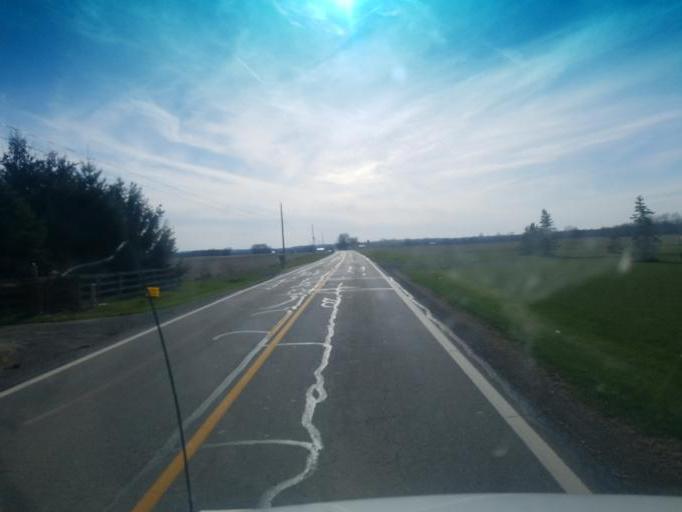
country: US
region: Ohio
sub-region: Champaign County
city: North Lewisburg
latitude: 40.3498
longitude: -83.5199
